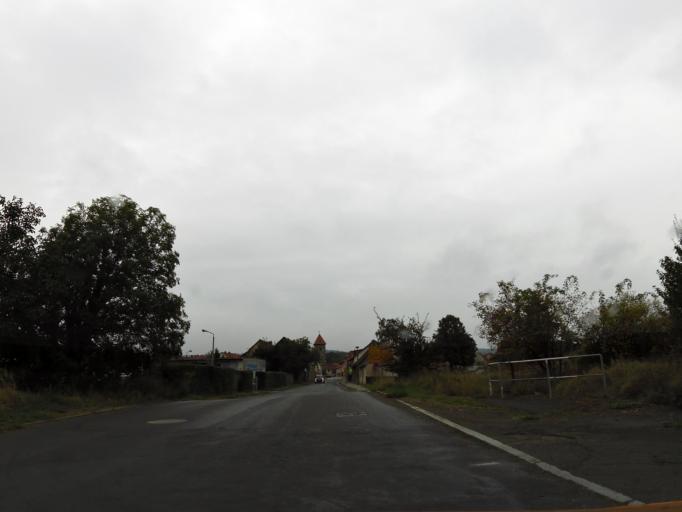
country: DE
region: Saxony-Anhalt
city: Ballenstedt
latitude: 51.7253
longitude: 11.2462
